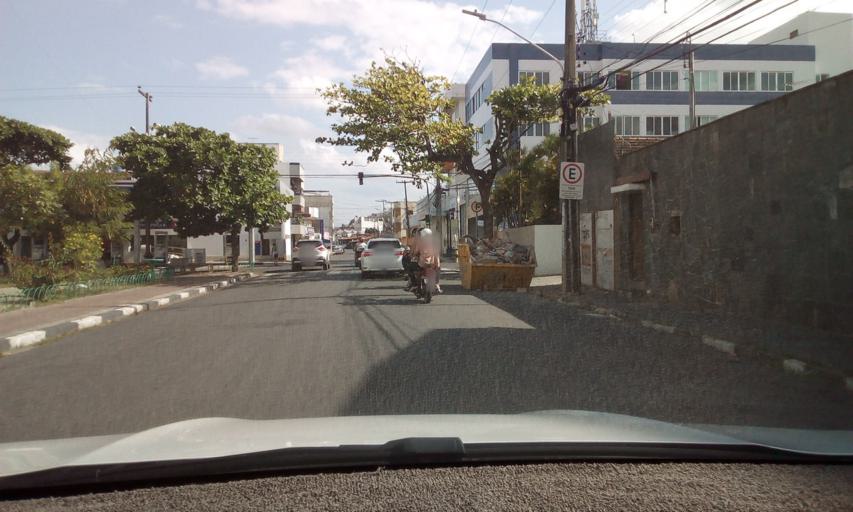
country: BR
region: Pernambuco
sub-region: Caruaru
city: Caruaru
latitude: -8.2750
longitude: -35.9754
